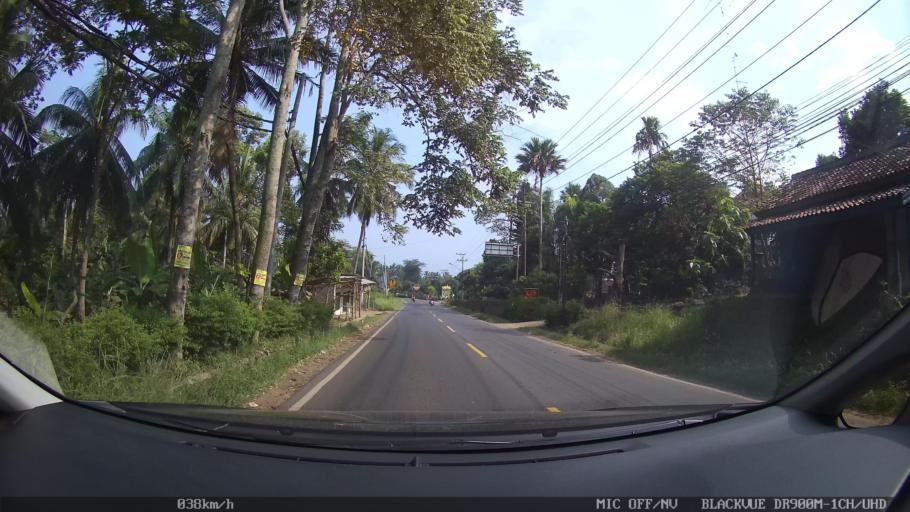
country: ID
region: Lampung
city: Natar
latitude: -5.3664
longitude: 105.1884
